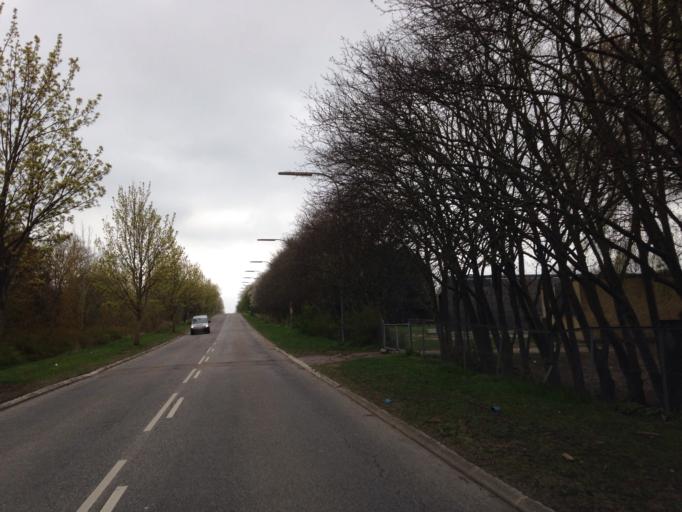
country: DK
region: Zealand
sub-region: Greve Kommune
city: Greve
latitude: 55.5933
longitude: 12.3228
